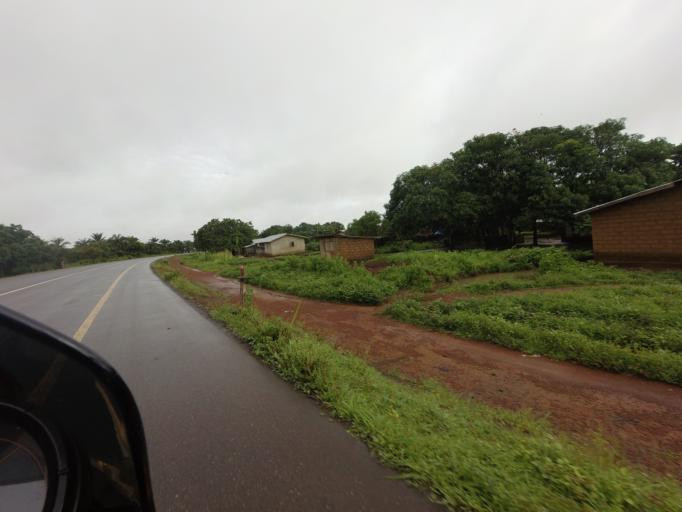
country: SL
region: Northern Province
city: Kambia
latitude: 9.1000
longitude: -12.9198
